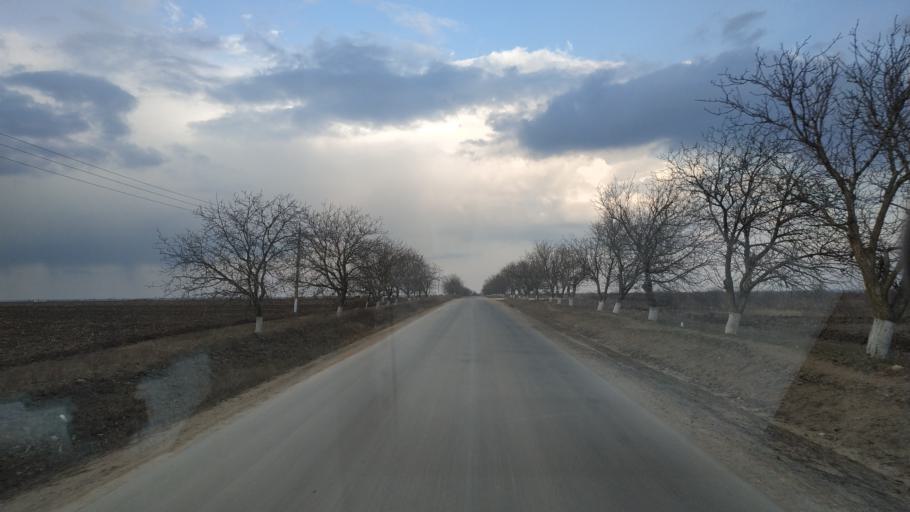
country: MD
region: Telenesti
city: Grigoriopol
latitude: 47.0235
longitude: 29.3220
